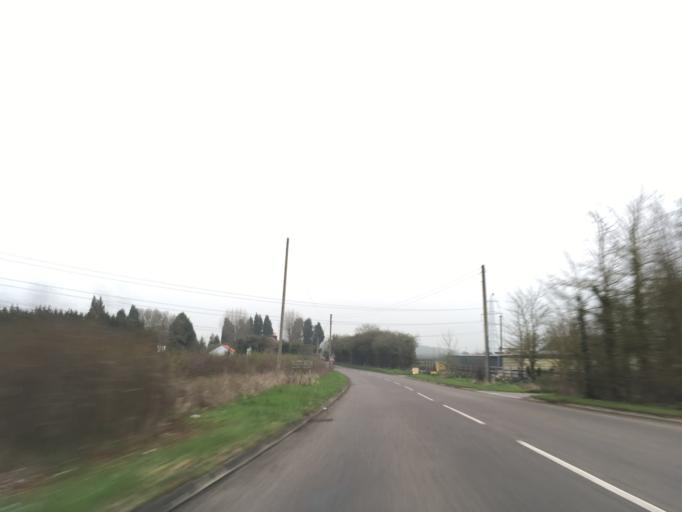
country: GB
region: England
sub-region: South Gloucestershire
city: Alveston
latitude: 51.5563
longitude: -2.5362
